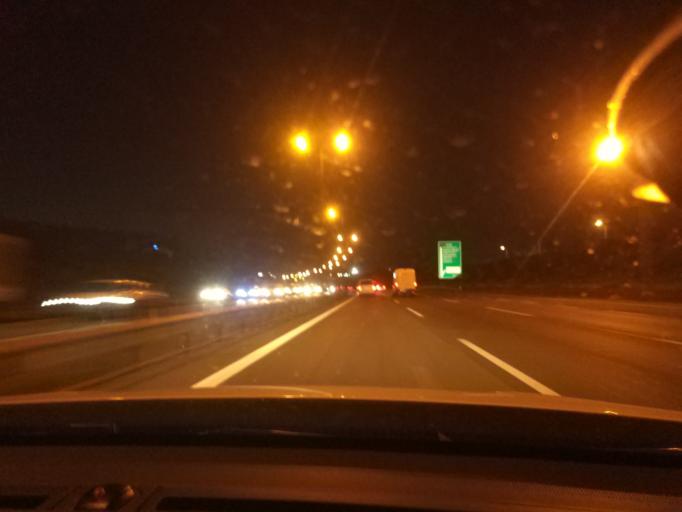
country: TR
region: Istanbul
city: Samandira
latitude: 40.9865
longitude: 29.1966
